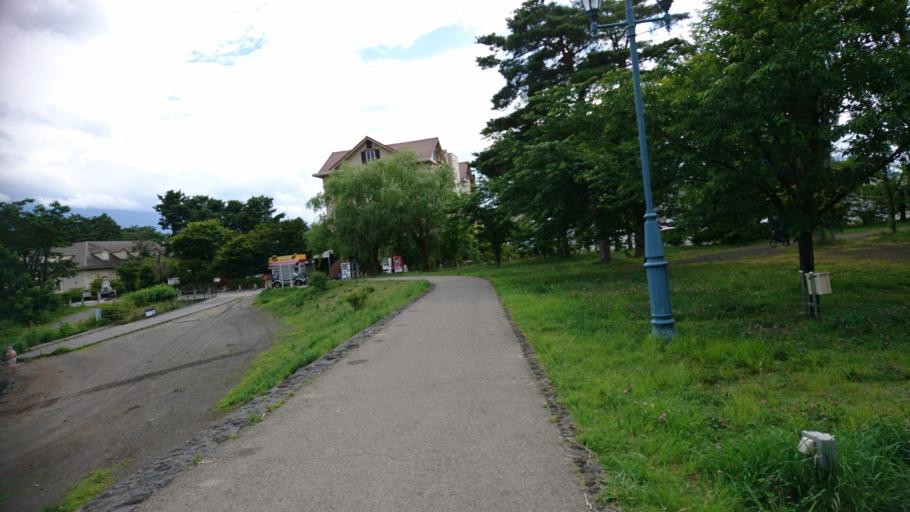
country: JP
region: Yamanashi
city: Fujikawaguchiko
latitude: 35.5069
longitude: 138.7633
